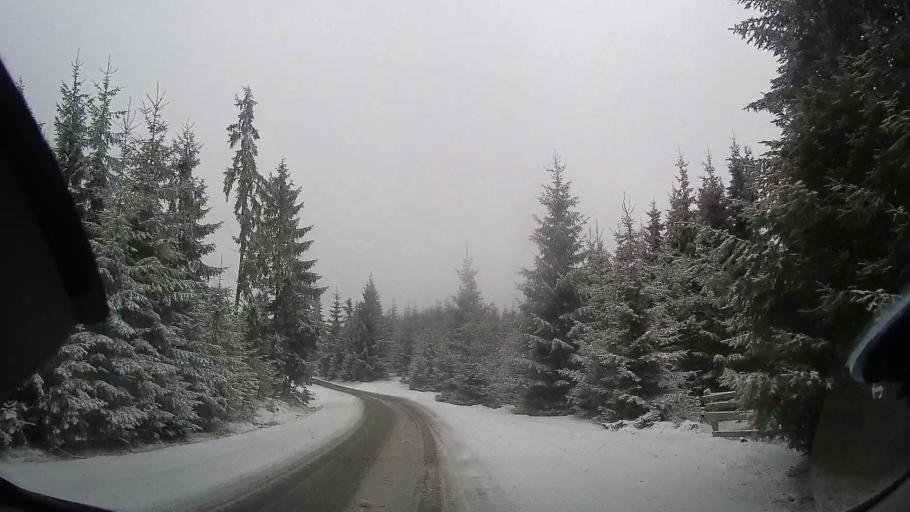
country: RO
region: Cluj
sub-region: Comuna Belis
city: Belis
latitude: 46.6442
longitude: 23.0691
